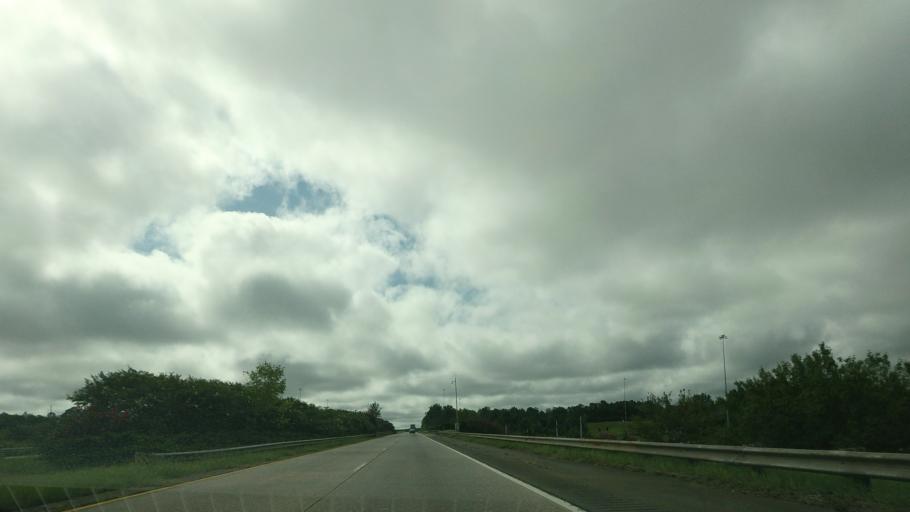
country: US
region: Georgia
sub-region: Bibb County
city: Macon
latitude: 32.8007
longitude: -83.5702
